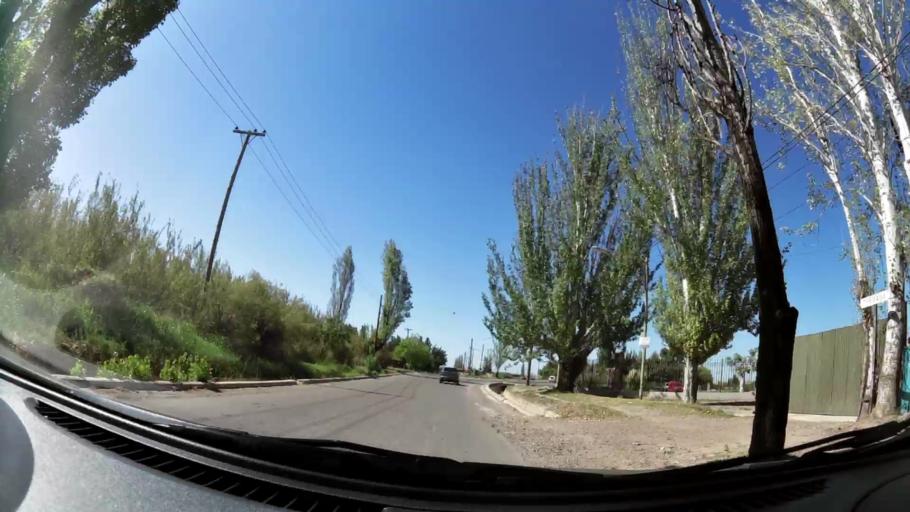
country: AR
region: Mendoza
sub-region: Departamento de Godoy Cruz
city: Godoy Cruz
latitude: -32.9717
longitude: -68.8363
